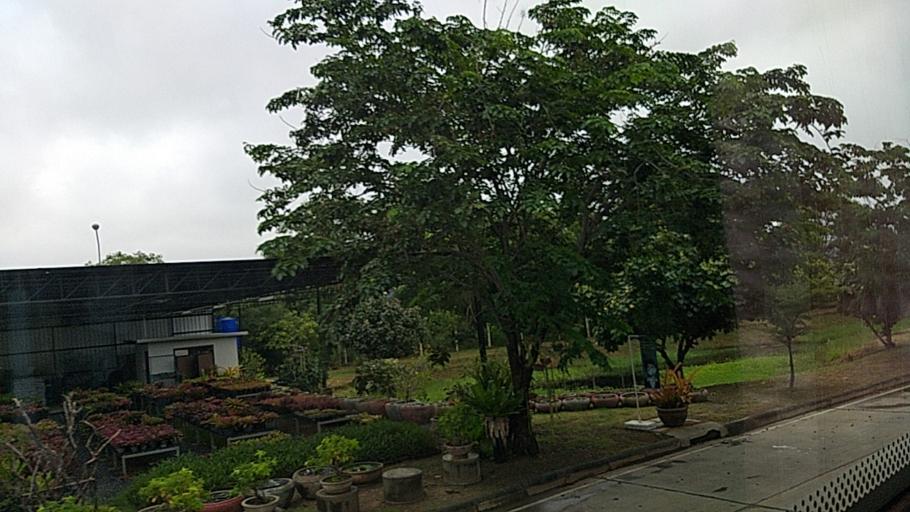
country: TH
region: Nakhon Ratchasima
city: Nakhon Ratchasima
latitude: 14.9937
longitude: 102.0923
